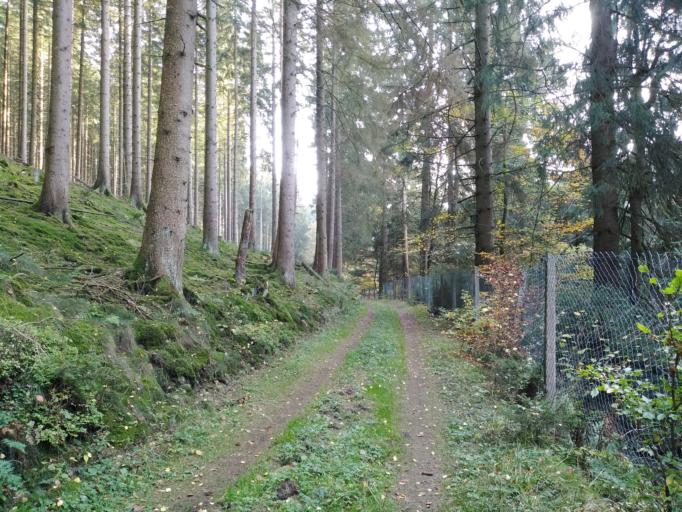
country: DE
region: North Rhine-Westphalia
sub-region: Regierungsbezirk Arnsberg
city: Brilon
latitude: 51.3577
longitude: 8.6186
